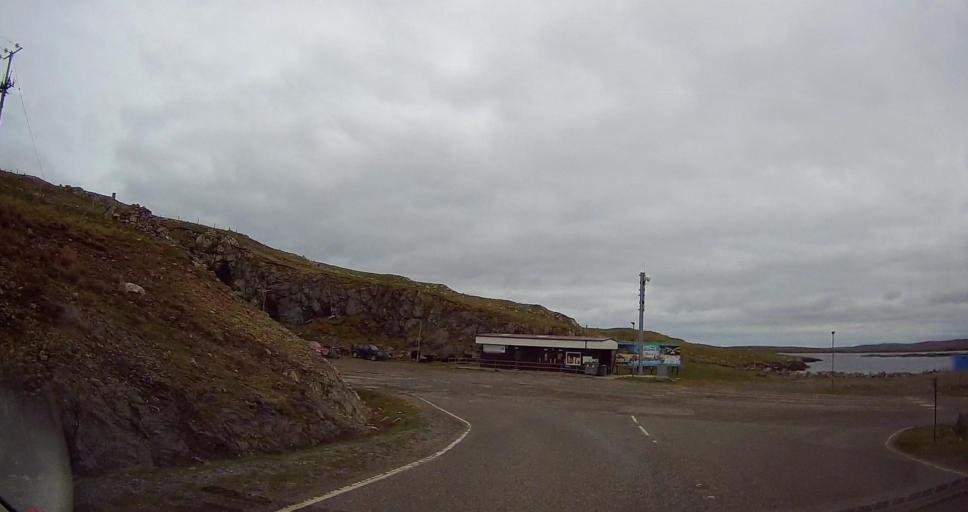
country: GB
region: Scotland
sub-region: Shetland Islands
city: Shetland
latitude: 60.6835
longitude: -0.9657
